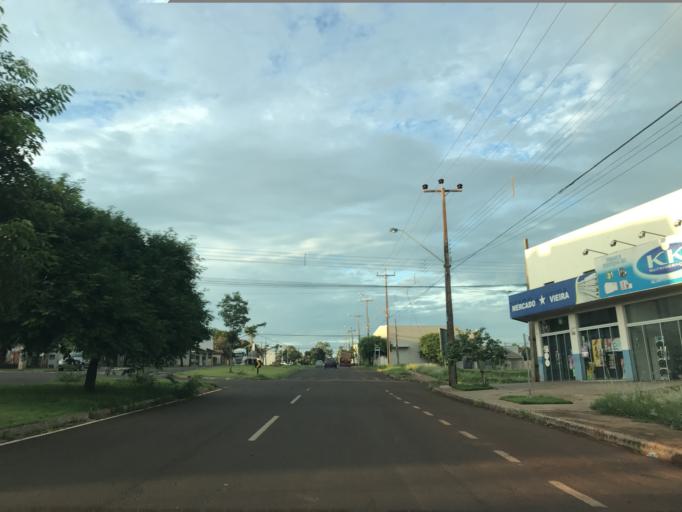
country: BR
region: Parana
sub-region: Maringa
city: Maringa
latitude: -23.3830
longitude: -51.9088
